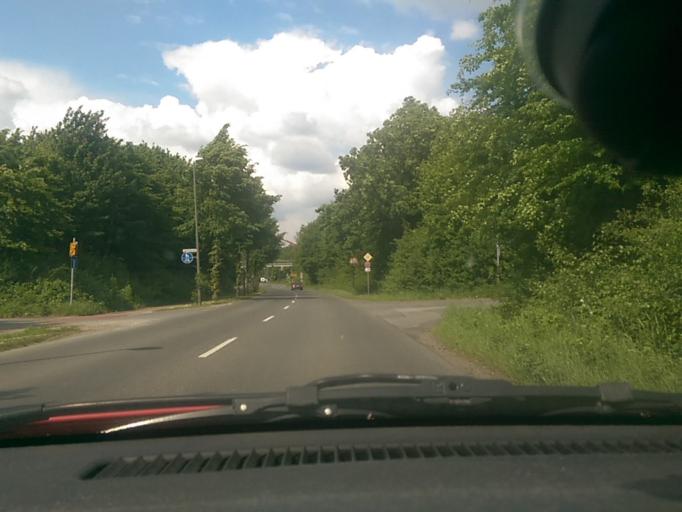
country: DE
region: North Rhine-Westphalia
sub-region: Regierungsbezirk Dusseldorf
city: Essen
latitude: 51.5188
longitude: 7.0452
